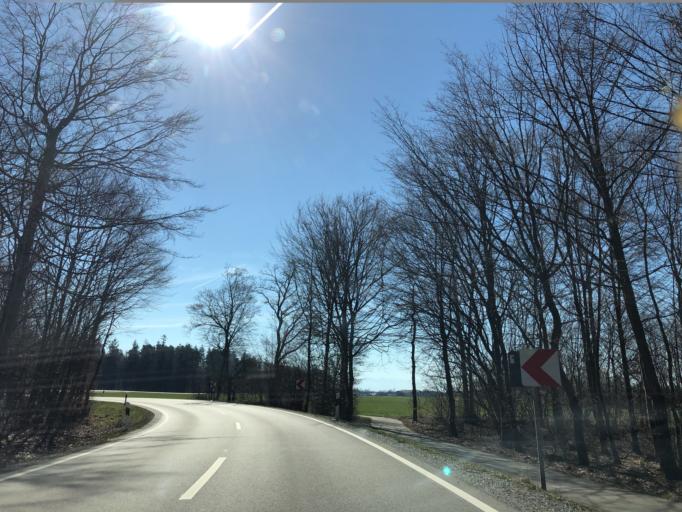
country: DE
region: Bavaria
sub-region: Upper Bavaria
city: Pfaffing
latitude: 48.0741
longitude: 12.1049
